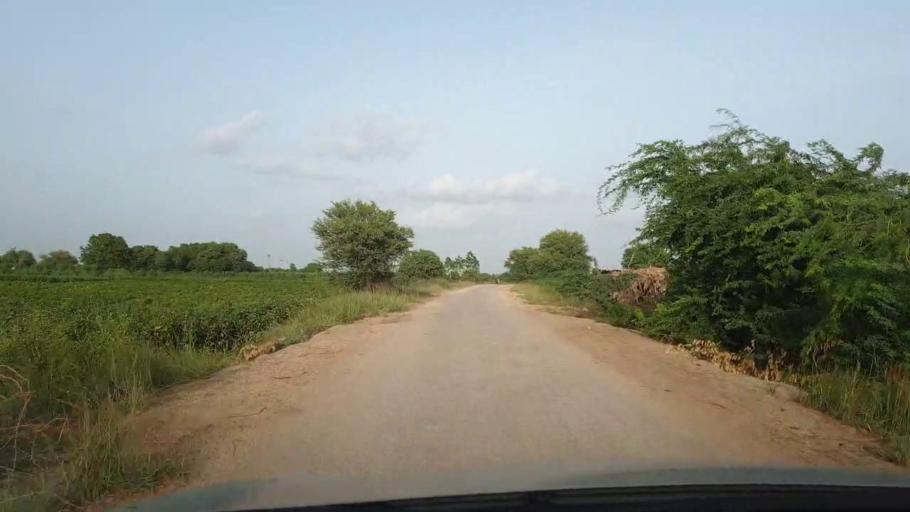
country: PK
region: Sindh
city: Tando Ghulam Ali
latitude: 25.0979
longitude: 68.8863
